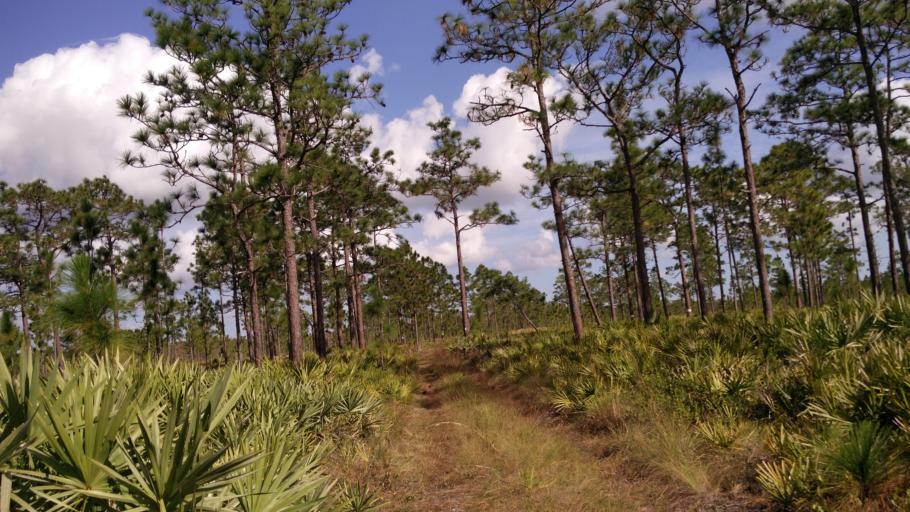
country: US
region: Florida
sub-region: Brevard County
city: June Park
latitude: 28.0495
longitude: -80.9658
